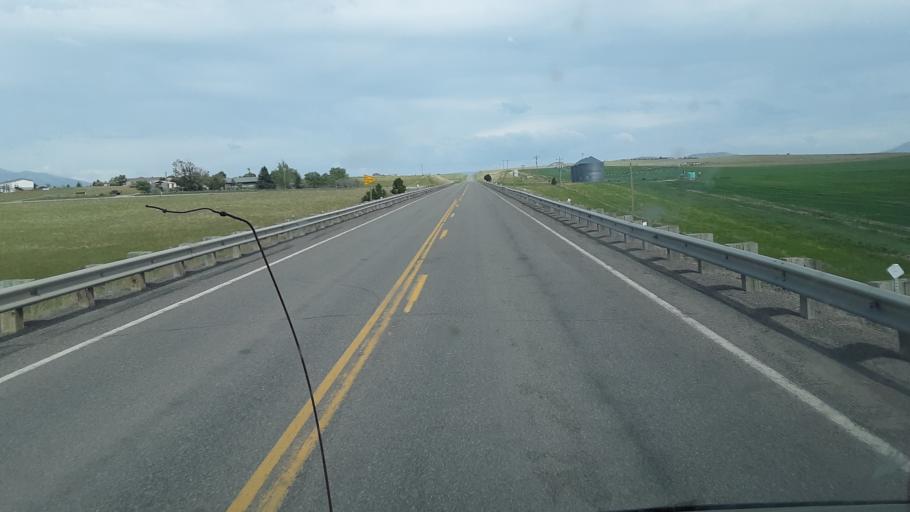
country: US
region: Montana
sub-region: Broadwater County
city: Townsend
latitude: 46.3212
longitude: -111.4553
